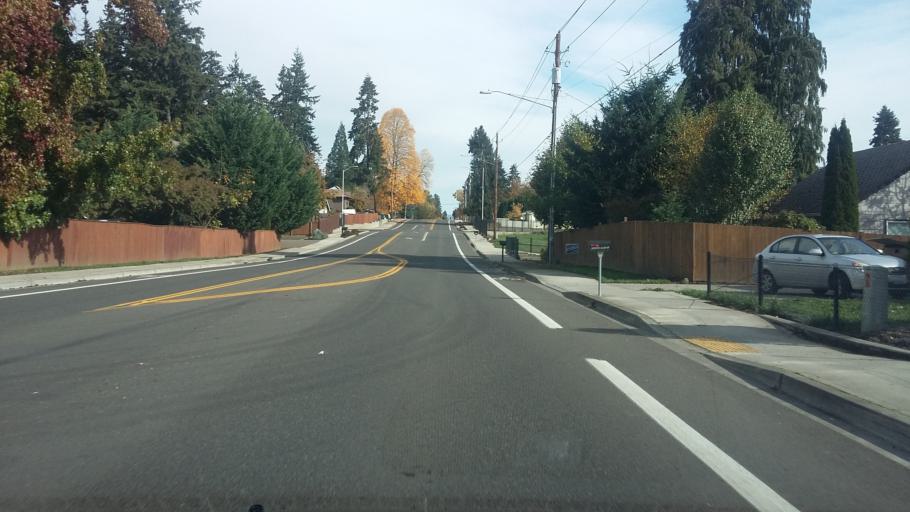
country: US
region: Washington
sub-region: Clark County
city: Hazel Dell
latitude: 45.6859
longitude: -122.6520
